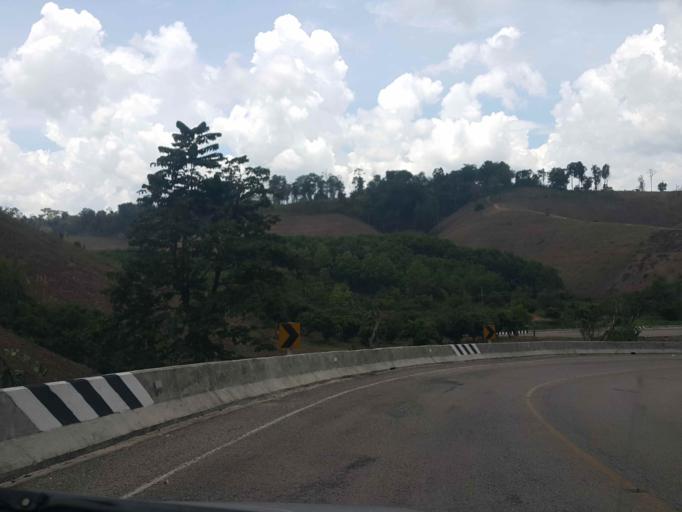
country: TH
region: Phayao
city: Chiang Muan
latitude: 18.9251
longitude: 100.1035
